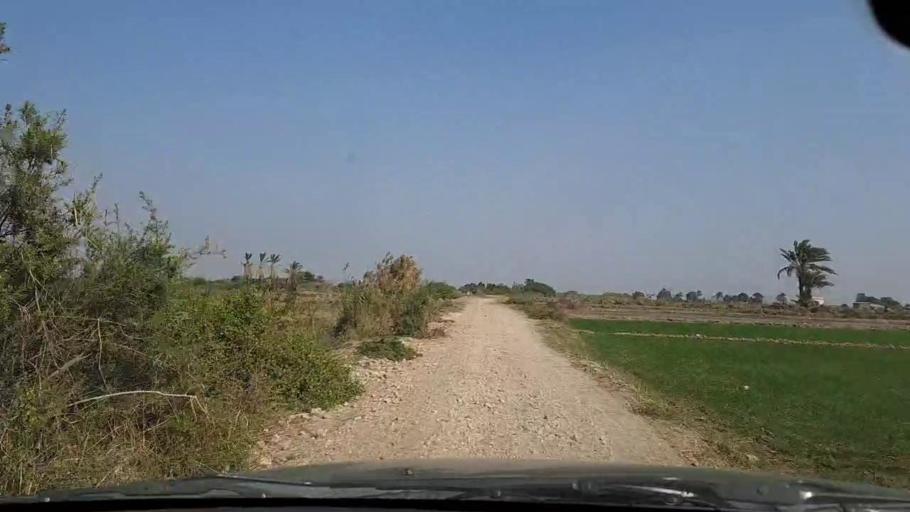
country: PK
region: Sindh
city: Mirpur Sakro
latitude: 24.3779
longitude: 67.6840
